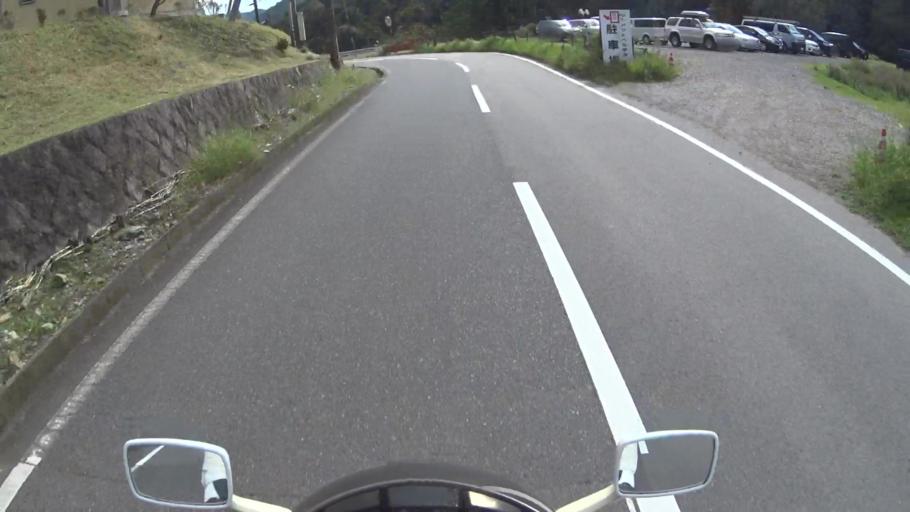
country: JP
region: Kyoto
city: Uji
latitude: 34.9311
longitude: 135.8566
